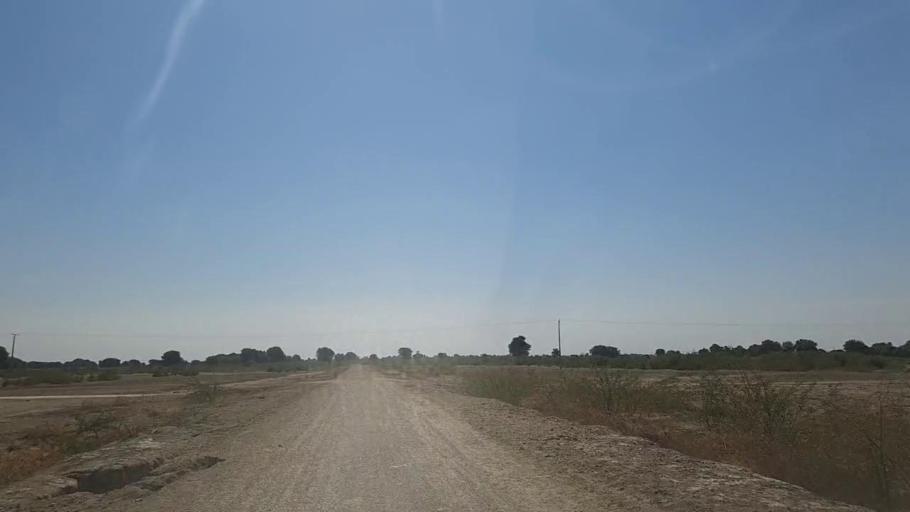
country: PK
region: Sindh
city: Dhoro Naro
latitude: 25.3567
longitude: 69.5325
